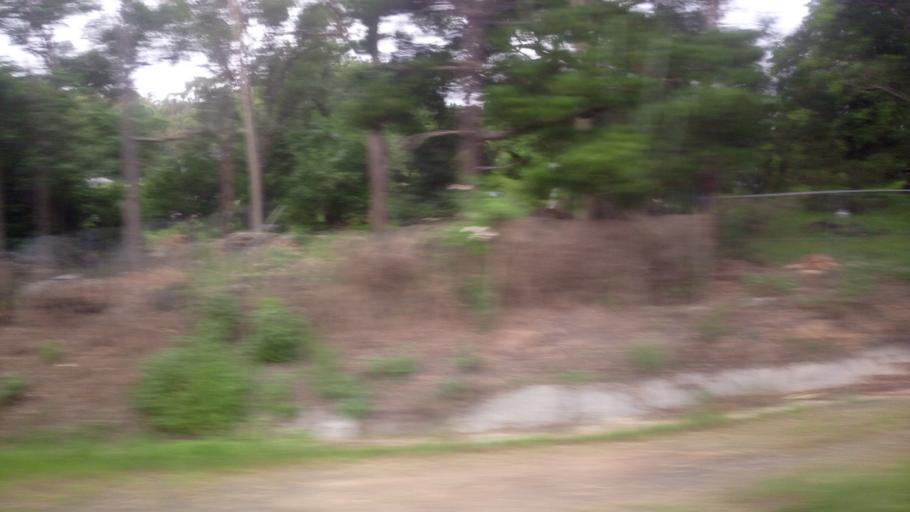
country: AU
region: New South Wales
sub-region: Blue Mountains Municipality
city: Glenbrook
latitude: -33.7740
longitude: 150.6220
